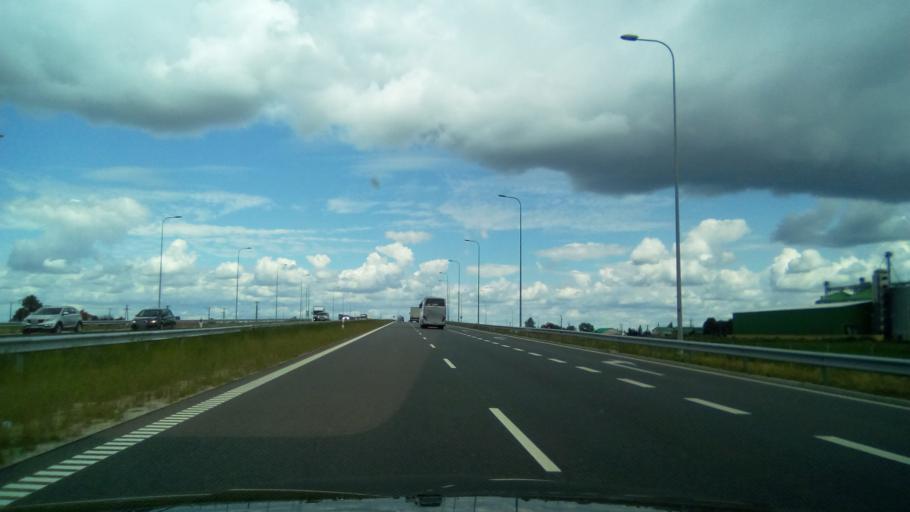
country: PL
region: Kujawsko-Pomorskie
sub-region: Powiat zninski
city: Znin
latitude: 52.8462
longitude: 17.6924
